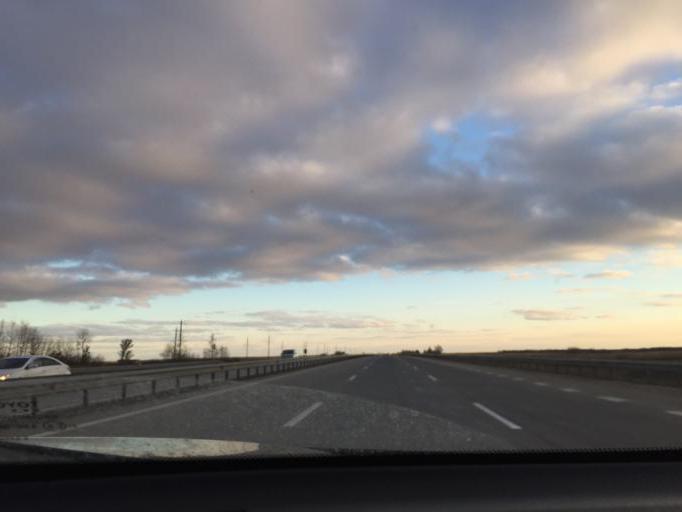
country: KZ
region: Astana Qalasy
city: Astana
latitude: 51.3529
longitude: 71.3357
